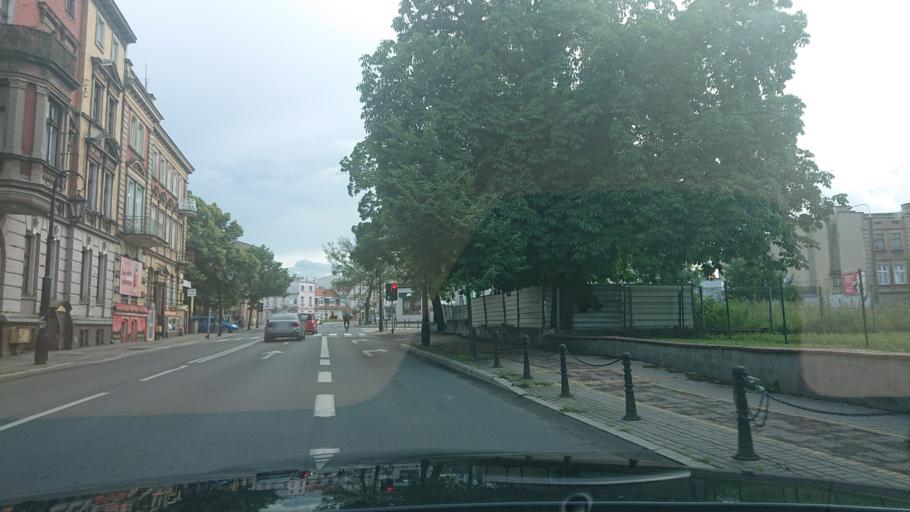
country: PL
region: Greater Poland Voivodeship
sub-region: Powiat gnieznienski
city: Gniezno
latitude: 52.5366
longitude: 17.6026
